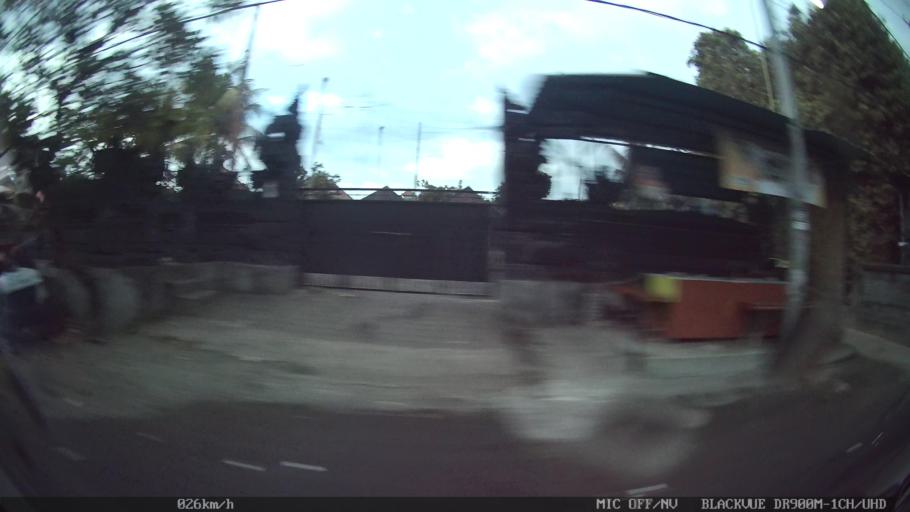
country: ID
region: Bali
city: Banjar Pasekan
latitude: -8.6256
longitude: 115.2795
